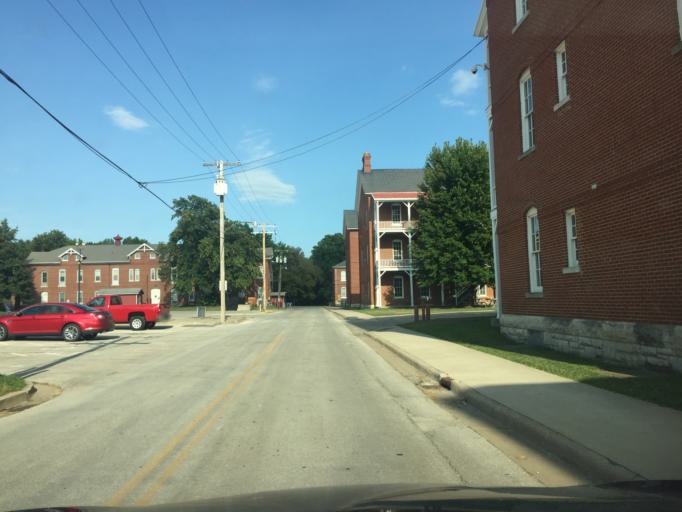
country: US
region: Kansas
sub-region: Leavenworth County
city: Leavenworth
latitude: 39.3562
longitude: -94.9214
